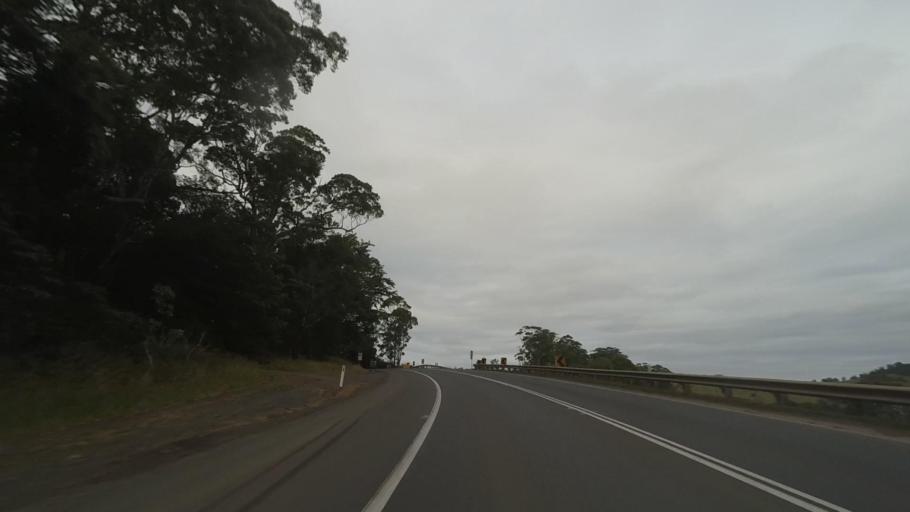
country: AU
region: New South Wales
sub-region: Shoalhaven Shire
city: Berry
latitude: -34.7568
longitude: 150.7474
